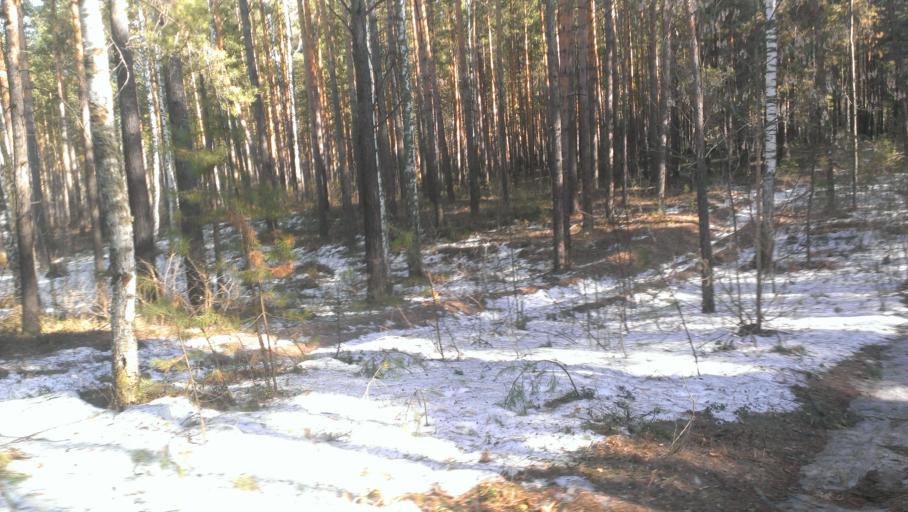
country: RU
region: Altai Krai
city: Yuzhnyy
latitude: 53.2831
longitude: 83.6970
